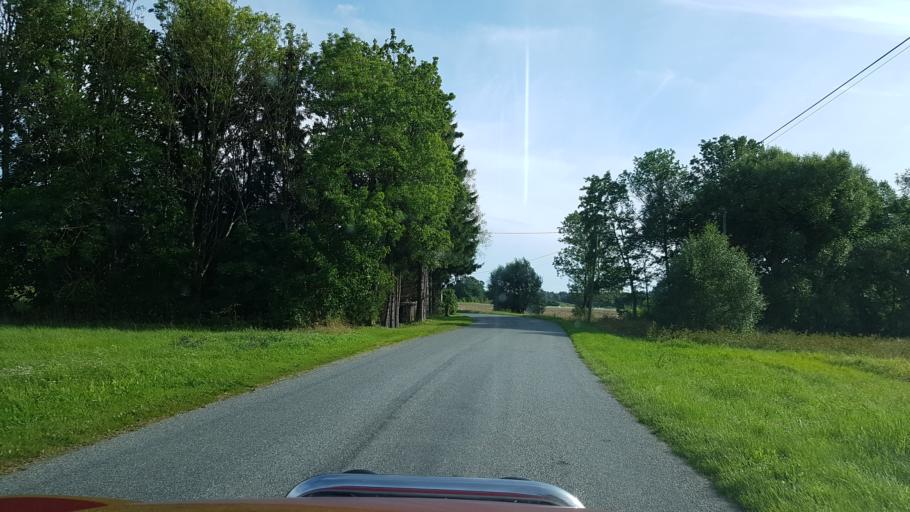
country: EE
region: Laeaene
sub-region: Lihula vald
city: Lihula
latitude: 58.4445
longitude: 24.0027
